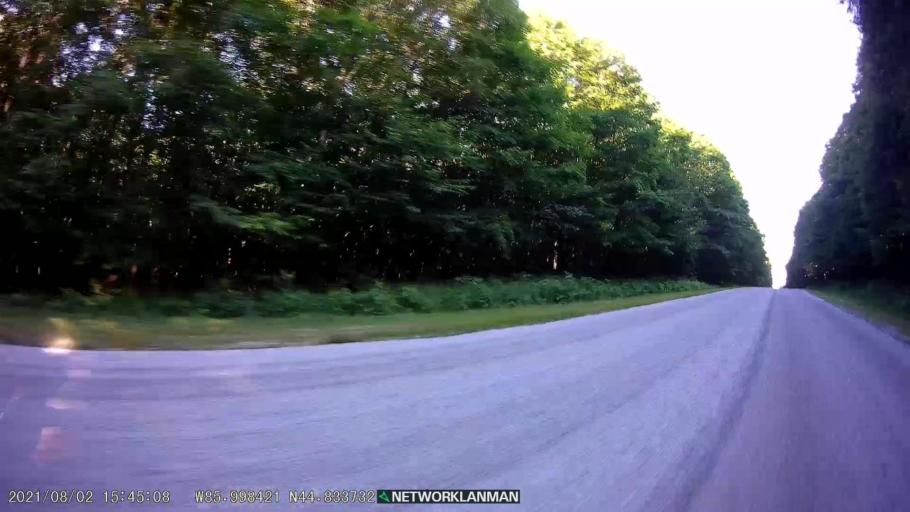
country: US
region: Michigan
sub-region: Benzie County
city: Beulah
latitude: 44.8335
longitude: -85.9986
